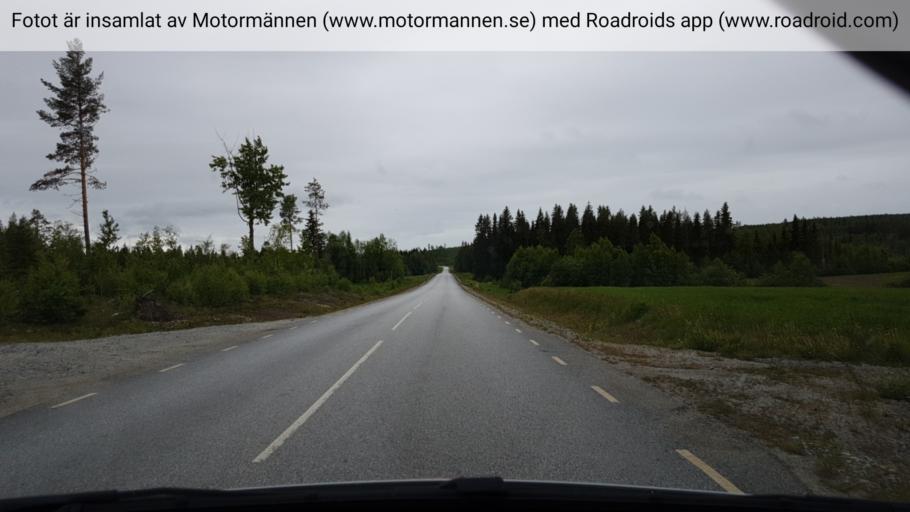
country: SE
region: Vaesterbotten
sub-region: Vindelns Kommun
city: Vindeln
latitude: 64.1944
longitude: 19.4114
